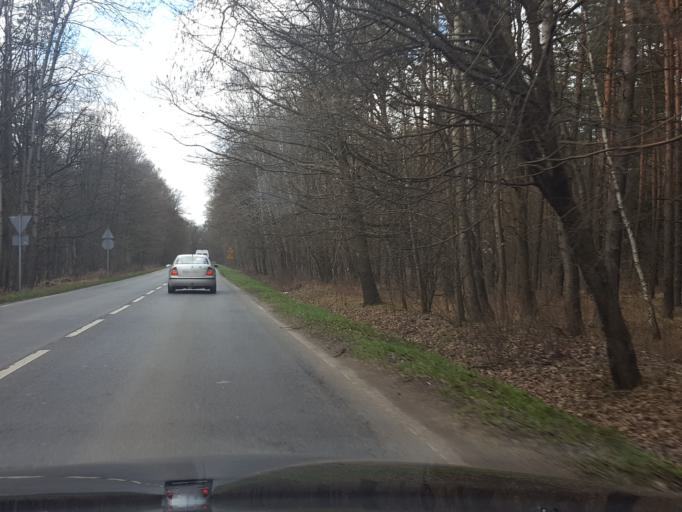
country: PL
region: Silesian Voivodeship
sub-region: Powiat pszczynski
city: Kobior
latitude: 50.0494
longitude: 18.9417
